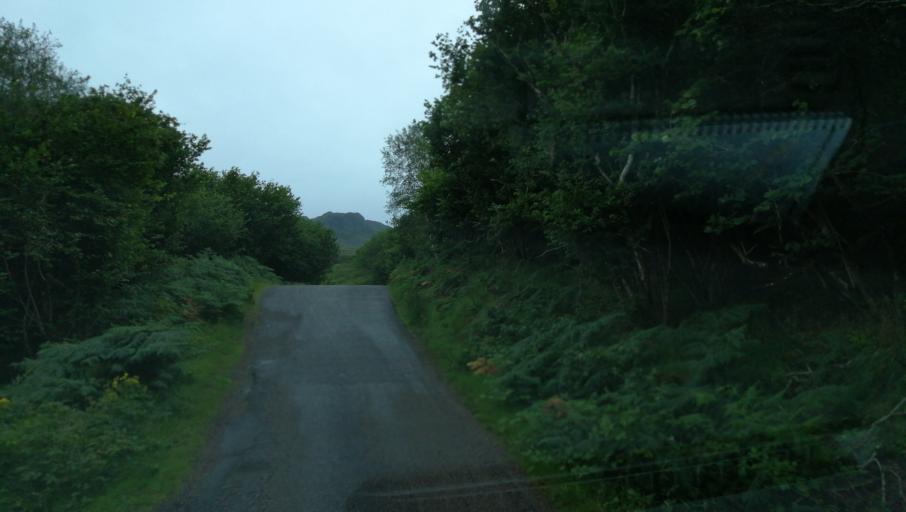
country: GB
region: Scotland
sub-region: Argyll and Bute
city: Isle Of Mull
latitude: 56.7212
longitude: -6.1701
